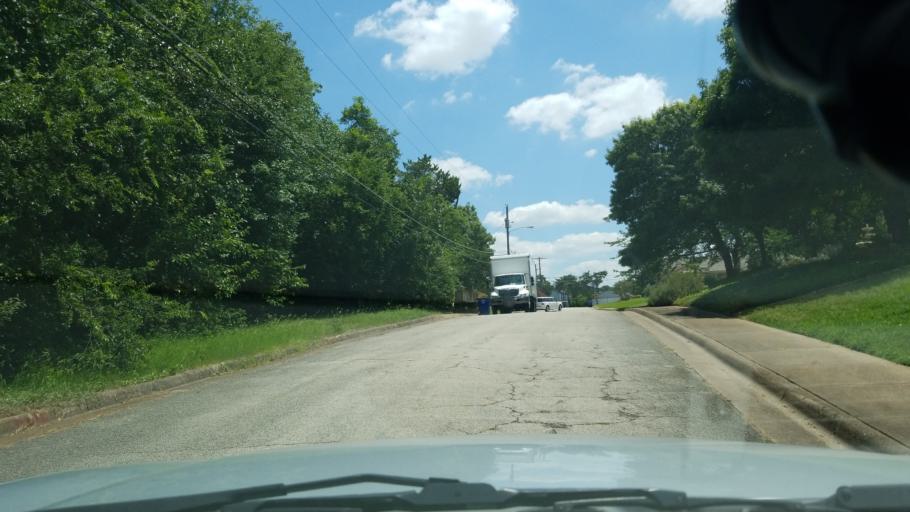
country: US
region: Texas
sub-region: Dallas County
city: Cockrell Hill
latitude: 32.6927
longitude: -96.8628
